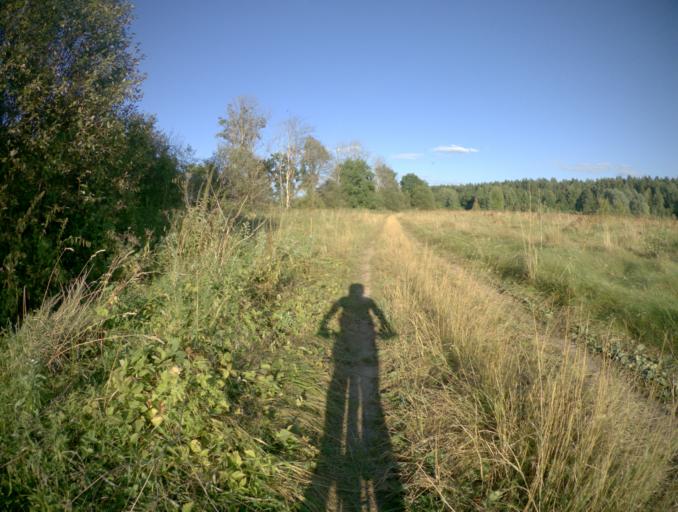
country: RU
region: Vladimir
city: Orgtrud
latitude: 56.1381
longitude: 40.7521
